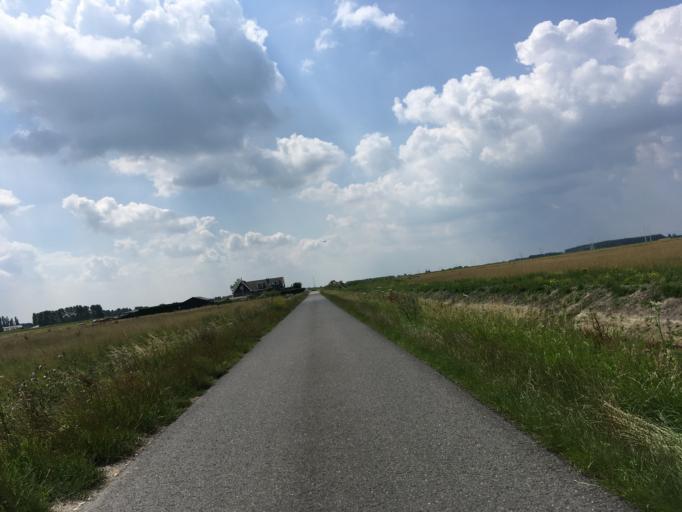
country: NL
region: North Holland
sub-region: Gemeente Velsen
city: Velsen-Zuid
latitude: 52.4215
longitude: 4.7247
